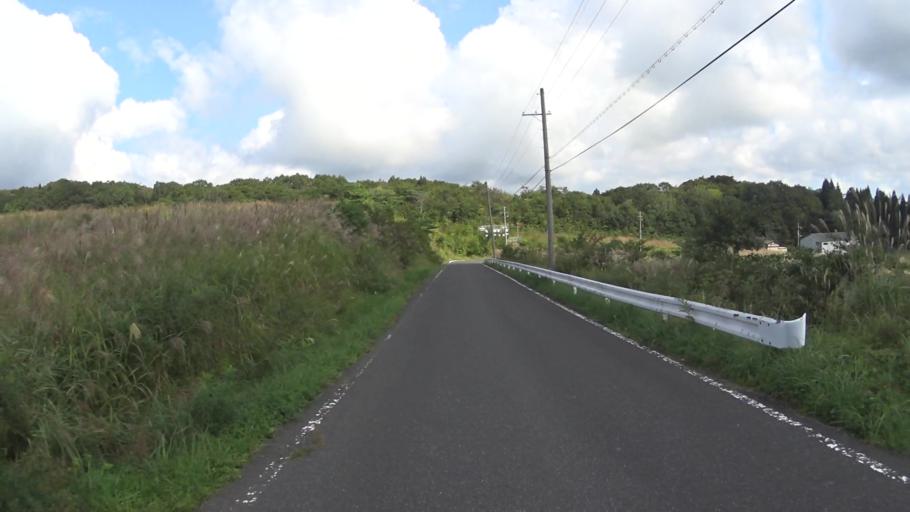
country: JP
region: Kyoto
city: Miyazu
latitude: 35.6543
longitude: 135.1810
